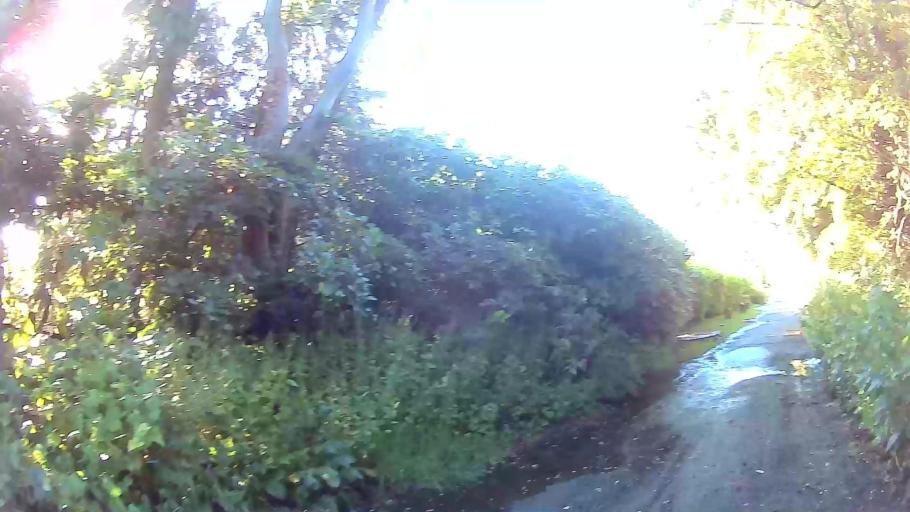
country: GB
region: England
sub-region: Essex
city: Writtle
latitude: 51.7388
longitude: 0.4405
